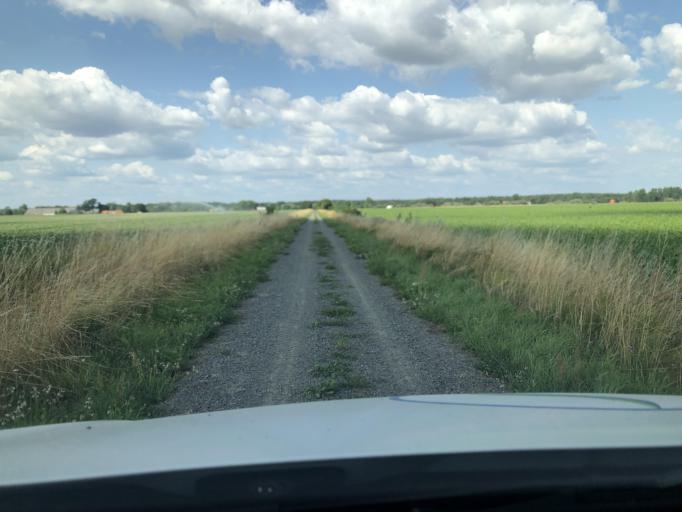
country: SE
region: Skane
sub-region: Kristianstads Kommun
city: Degeberga
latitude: 55.8890
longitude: 14.0809
